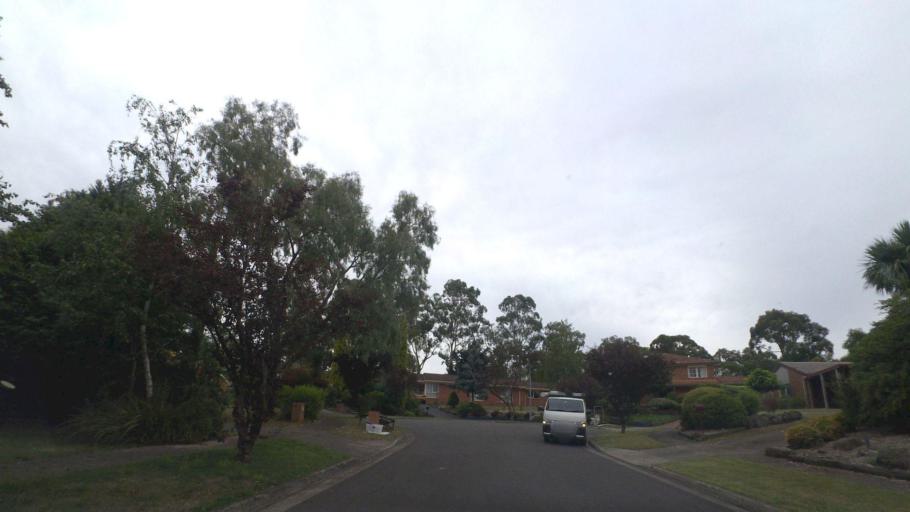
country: AU
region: Victoria
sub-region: Yarra Ranges
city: Lilydale
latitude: -37.7766
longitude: 145.3374
